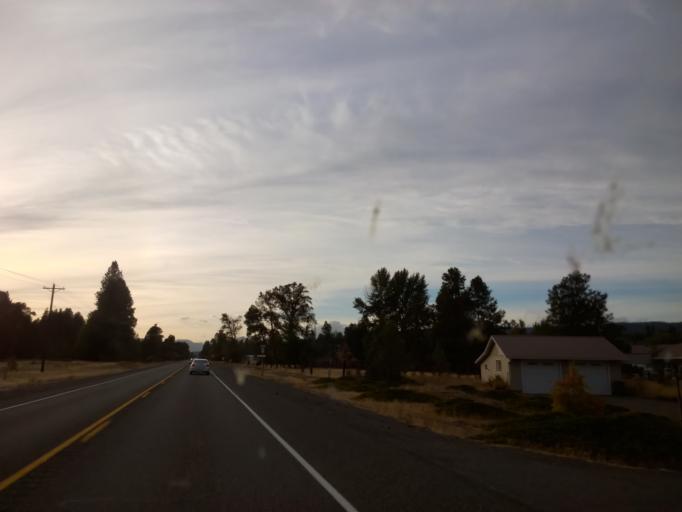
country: US
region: Washington
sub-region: Kittitas County
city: Cle Elum
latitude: 47.1761
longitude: -120.8606
